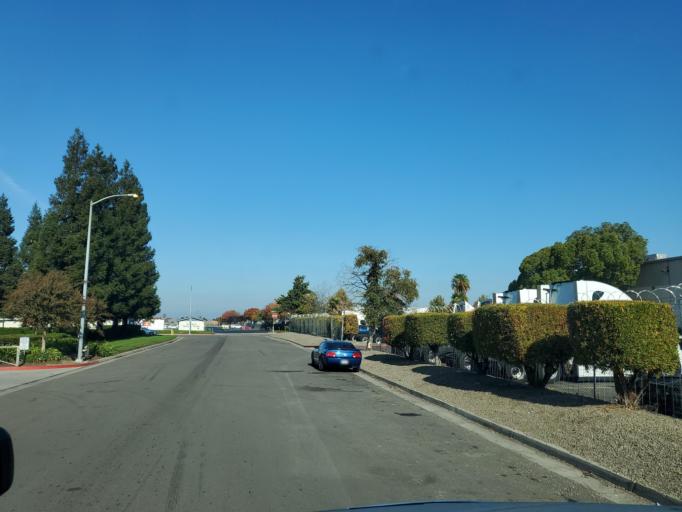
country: US
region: California
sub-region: San Joaquin County
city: Kennedy
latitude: 37.9100
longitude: -121.2332
